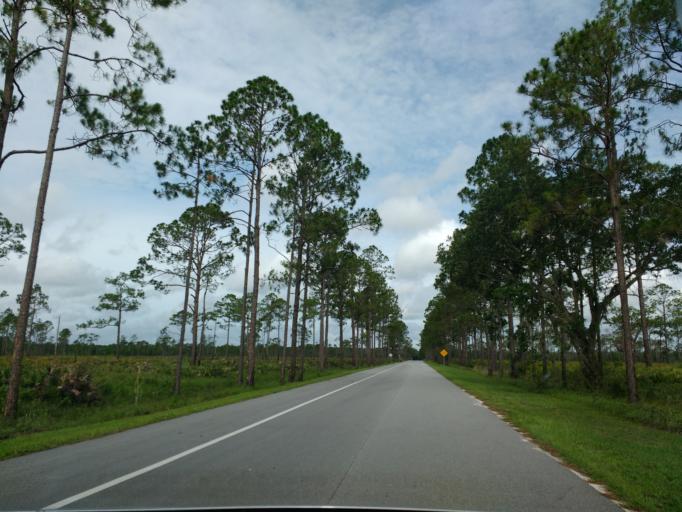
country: US
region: Florida
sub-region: Highlands County
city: Sebring
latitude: 27.4709
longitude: -81.5193
